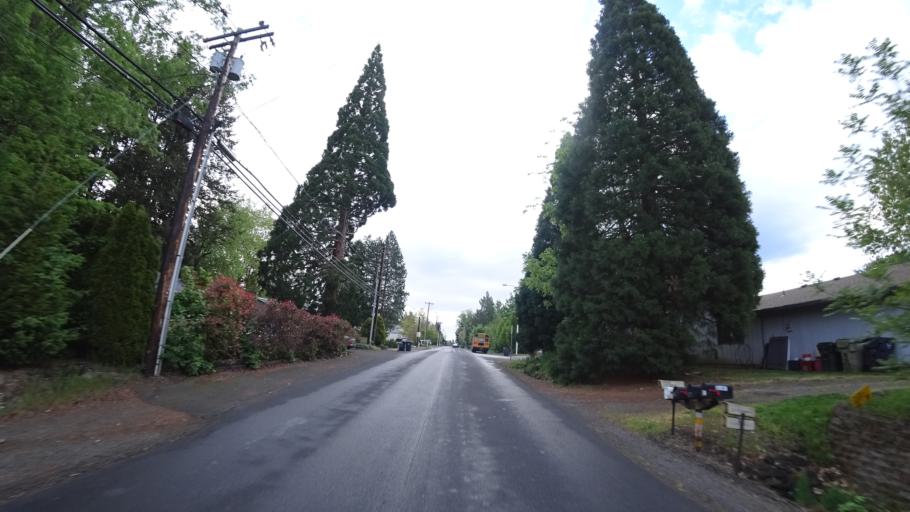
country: US
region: Oregon
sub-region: Washington County
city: Aloha
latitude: 45.5003
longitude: -122.8732
